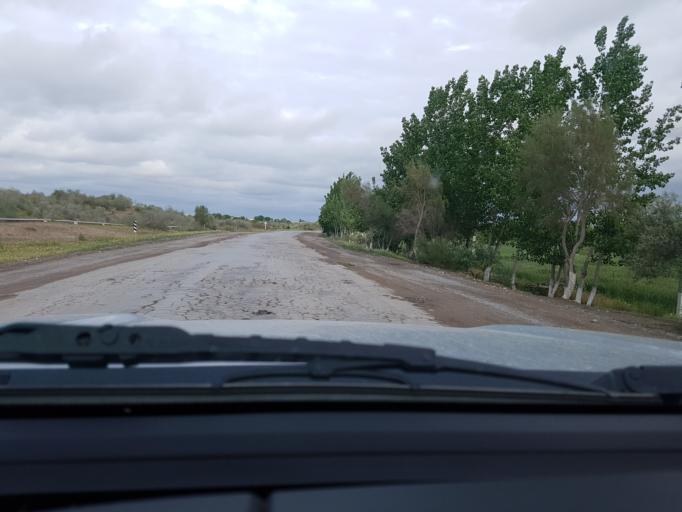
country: TM
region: Lebap
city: Atamyrat
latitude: 38.1131
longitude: 64.7330
